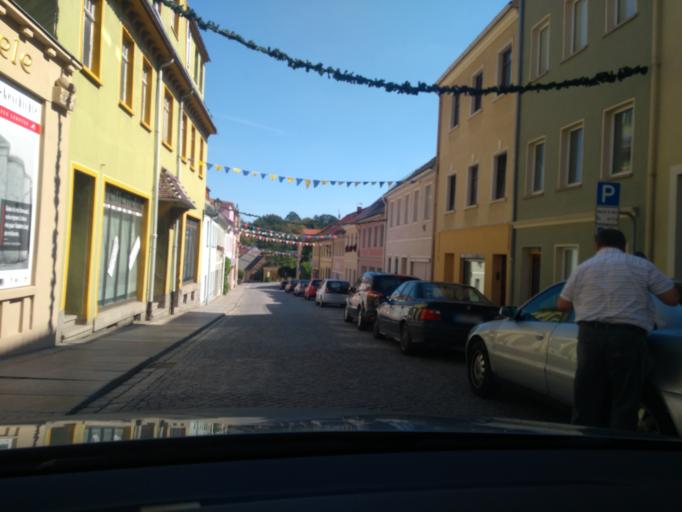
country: DE
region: Saxony
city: Kamenz
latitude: 51.2713
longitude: 14.0994
